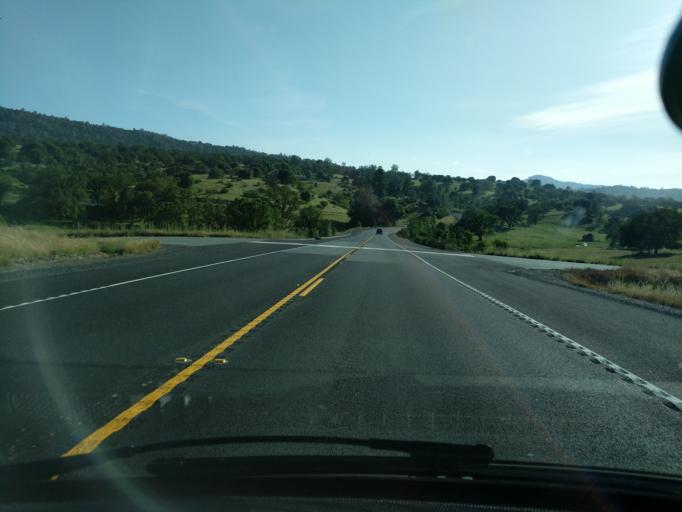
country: US
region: California
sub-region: Calaveras County
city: Angels Camp
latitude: 38.0712
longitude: -120.5889
